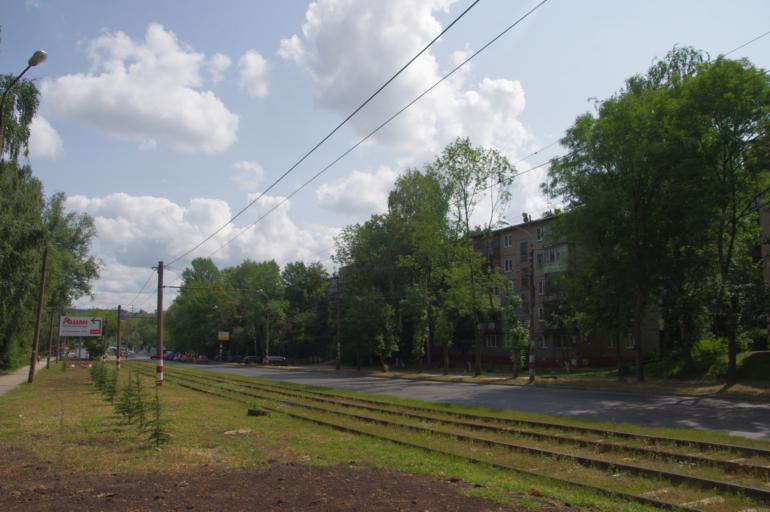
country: RU
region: Nizjnij Novgorod
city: Nizhniy Novgorod
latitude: 56.3019
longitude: 44.0384
